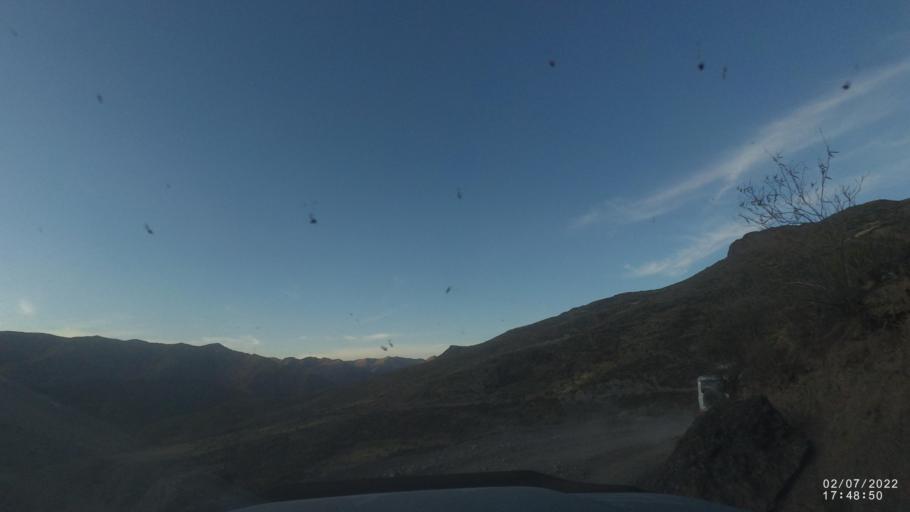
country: BO
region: Cochabamba
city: Irpa Irpa
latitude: -17.8515
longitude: -66.6187
